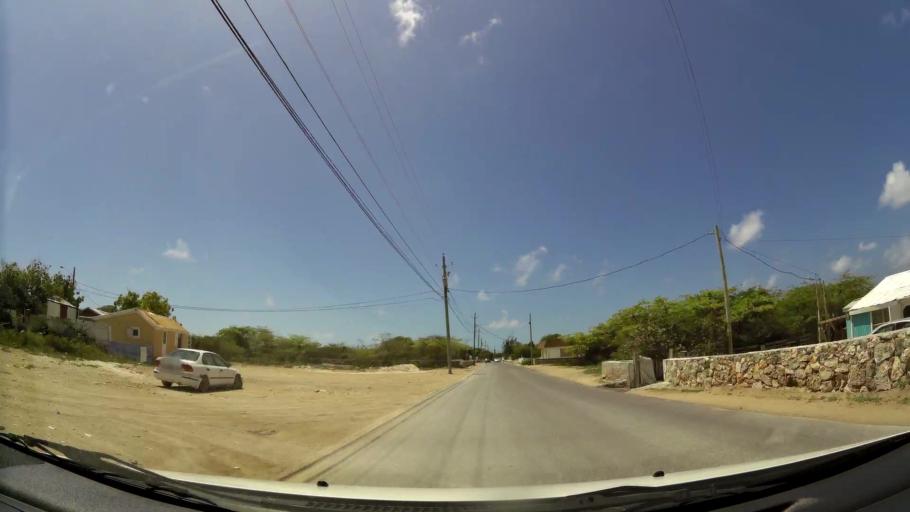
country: TC
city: Cockburn Town
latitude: 21.4766
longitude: -71.1455
